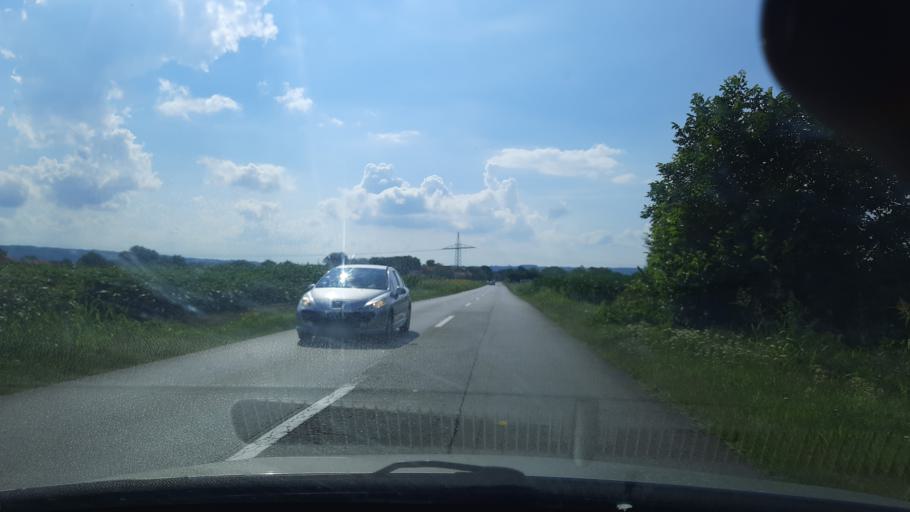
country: RS
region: Central Serbia
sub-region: Branicevski Okrug
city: Malo Crnice
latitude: 44.5865
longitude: 21.2841
